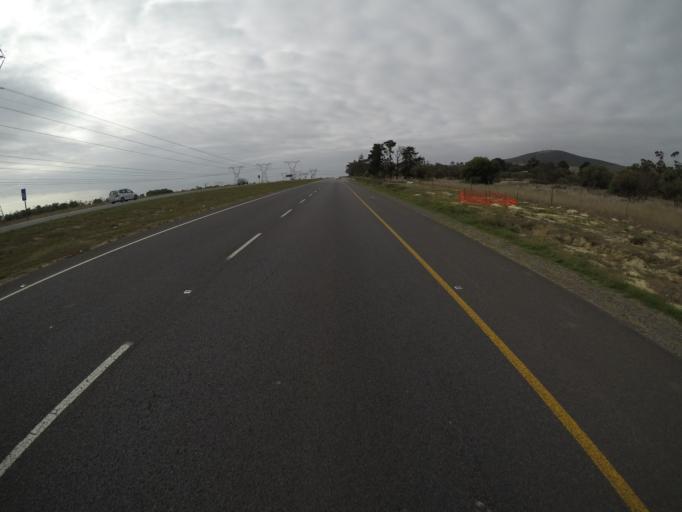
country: ZA
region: Western Cape
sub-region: City of Cape Town
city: Sunset Beach
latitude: -33.7311
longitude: 18.5450
